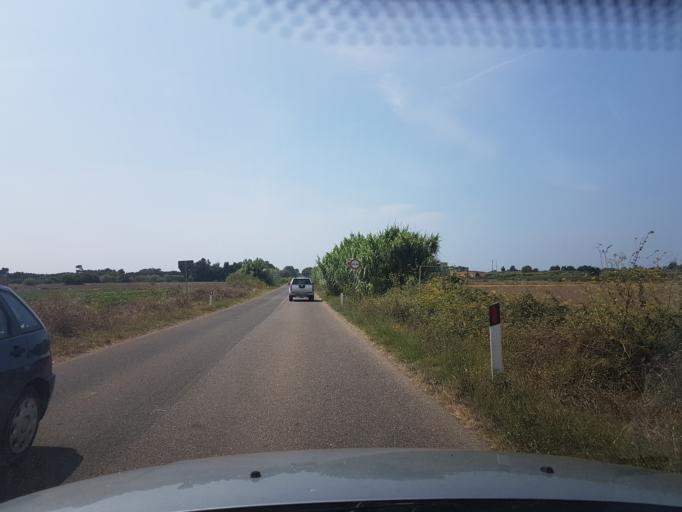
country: IT
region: Sardinia
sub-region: Provincia di Oristano
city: Solanas
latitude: 39.9183
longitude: 8.5528
